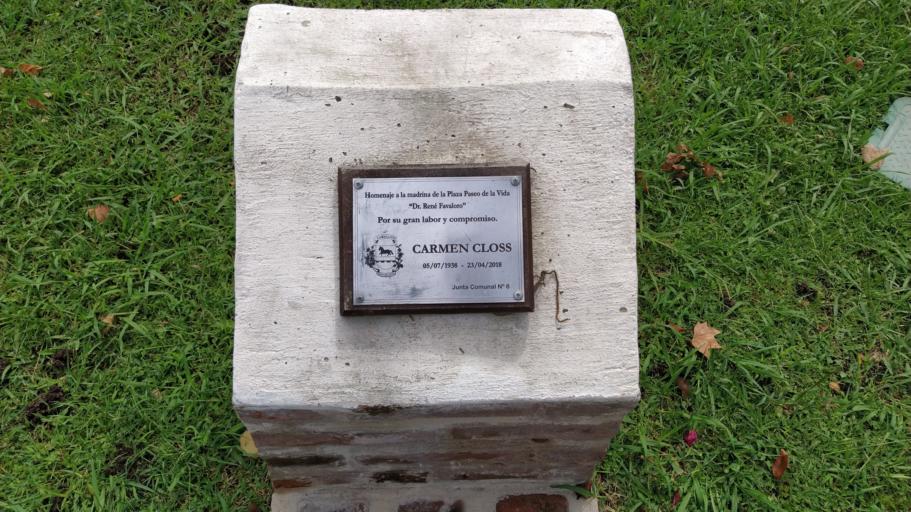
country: AR
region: Buenos Aires F.D.
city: Villa Santa Rita
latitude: -34.6189
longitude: -58.4436
